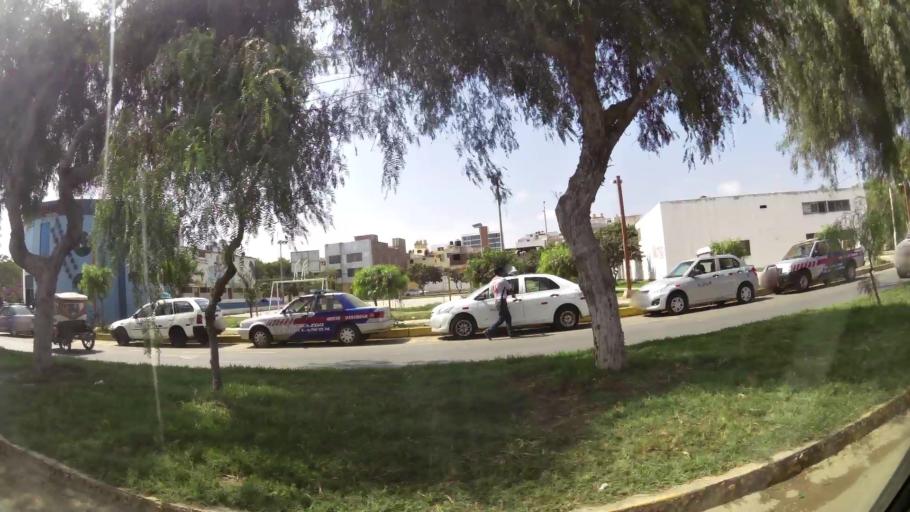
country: PE
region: La Libertad
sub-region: Provincia de Trujillo
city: Buenos Aires
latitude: -8.1352
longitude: -79.0443
